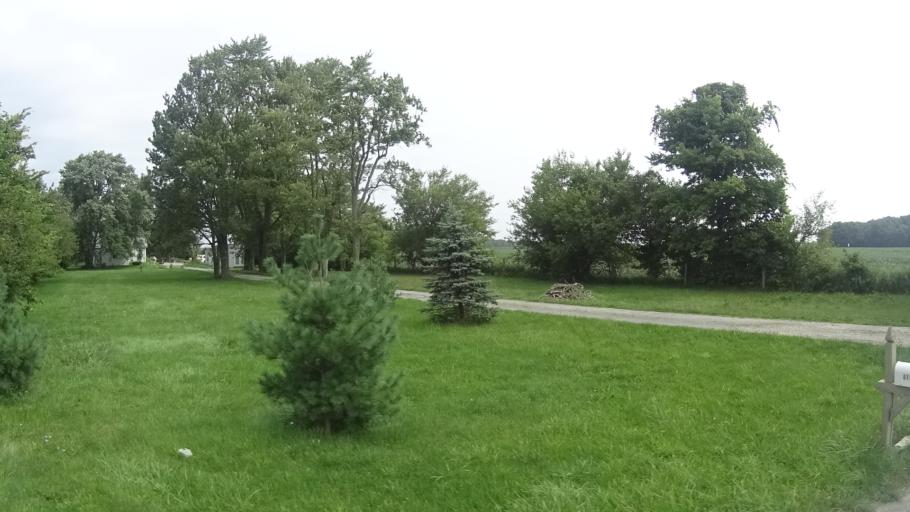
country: US
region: Indiana
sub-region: Madison County
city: Pendleton
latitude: 40.0314
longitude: -85.7891
